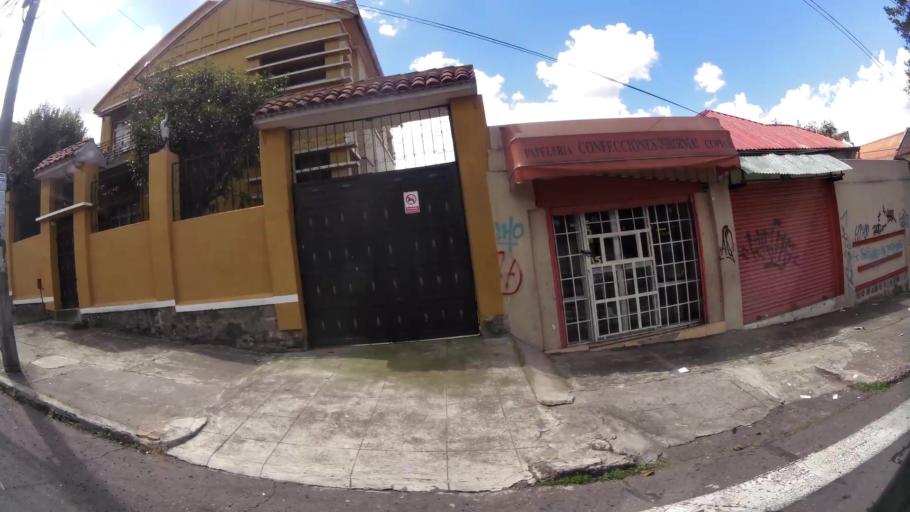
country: EC
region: Pichincha
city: Quito
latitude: -0.1900
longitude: -78.5029
